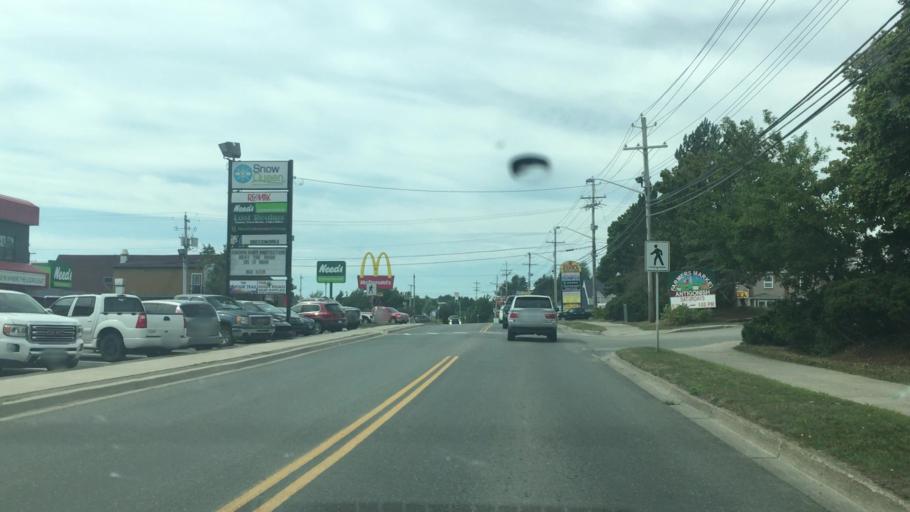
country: CA
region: Nova Scotia
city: Antigonish
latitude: 45.6160
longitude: -62.0010
